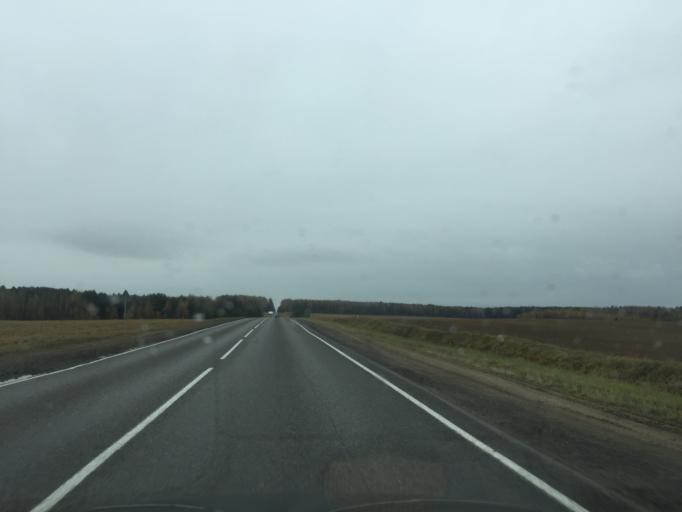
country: BY
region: Mogilev
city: Cherykaw
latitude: 53.6541
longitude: 31.2565
